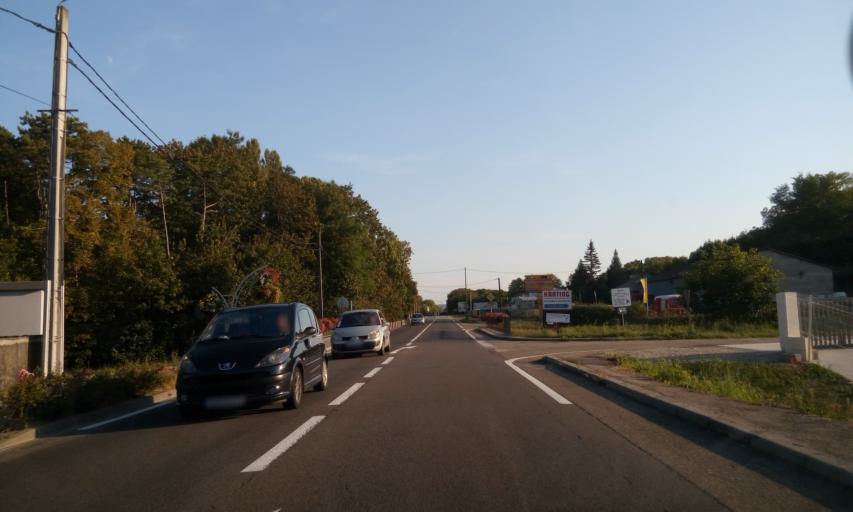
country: FR
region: Rhone-Alpes
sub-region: Departement de l'Ain
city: Ambronay
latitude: 46.0439
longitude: 5.3364
